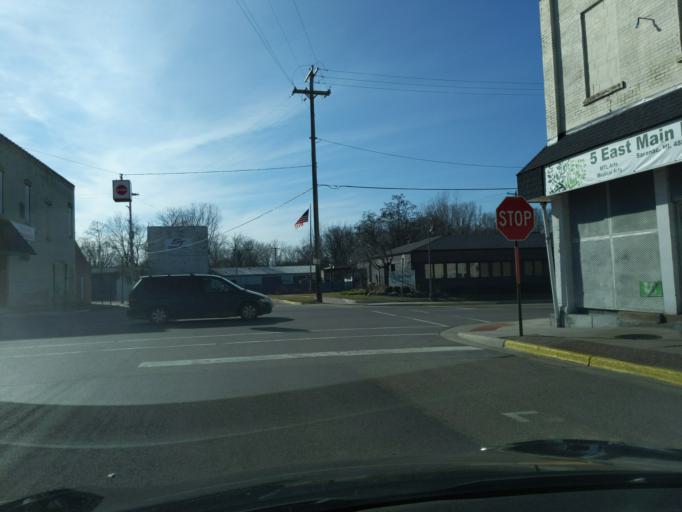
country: US
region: Michigan
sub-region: Ionia County
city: Saranac
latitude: 42.9312
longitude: -85.2130
